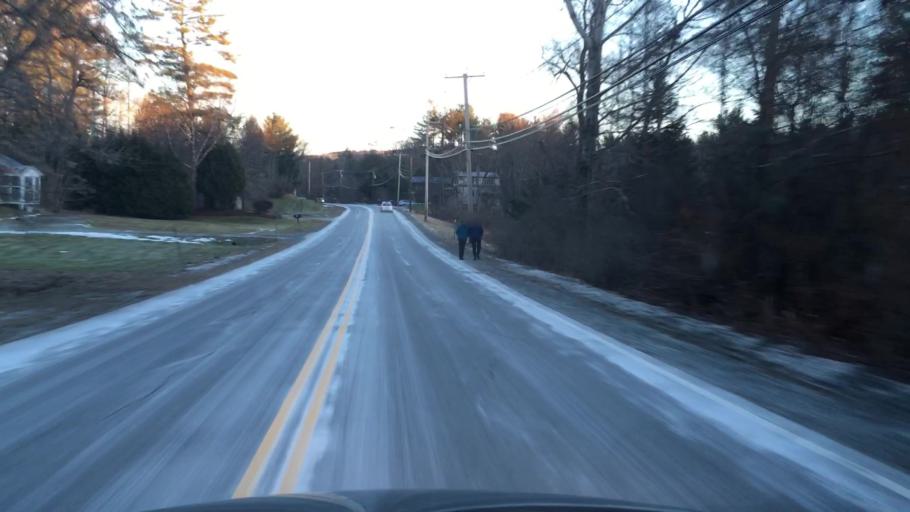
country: US
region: New Hampshire
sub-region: Grafton County
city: Hanover
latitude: 43.6912
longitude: -72.2625
